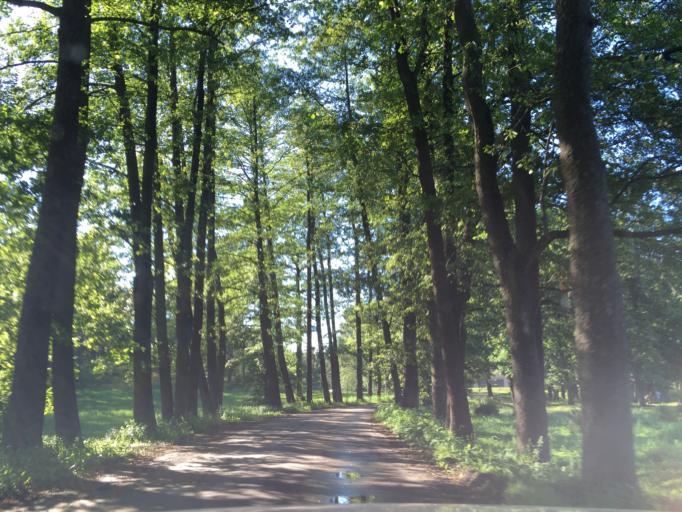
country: LV
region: Riga
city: Jaunciems
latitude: 57.0627
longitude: 24.1371
